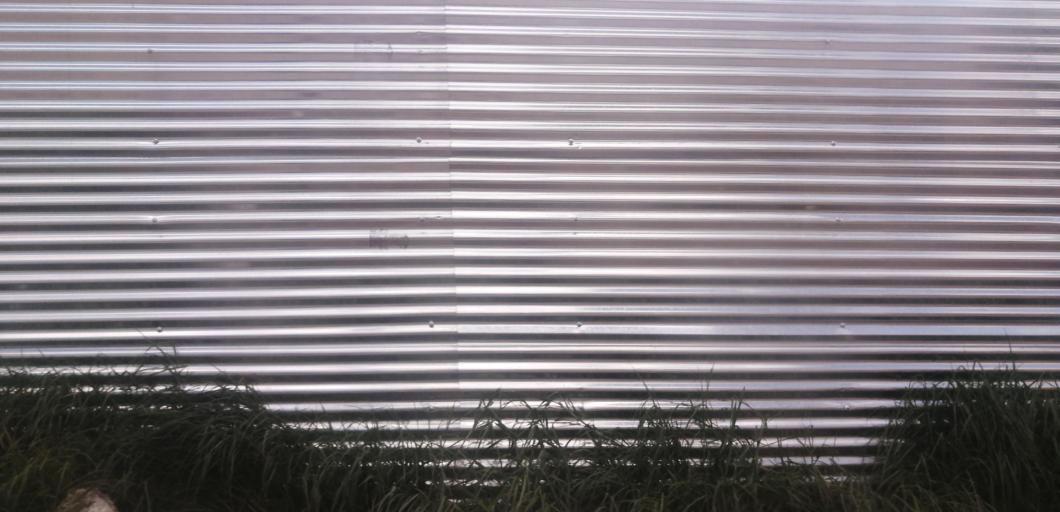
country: GT
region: Quetzaltenango
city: Quetzaltenango
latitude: 14.8343
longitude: -91.5334
